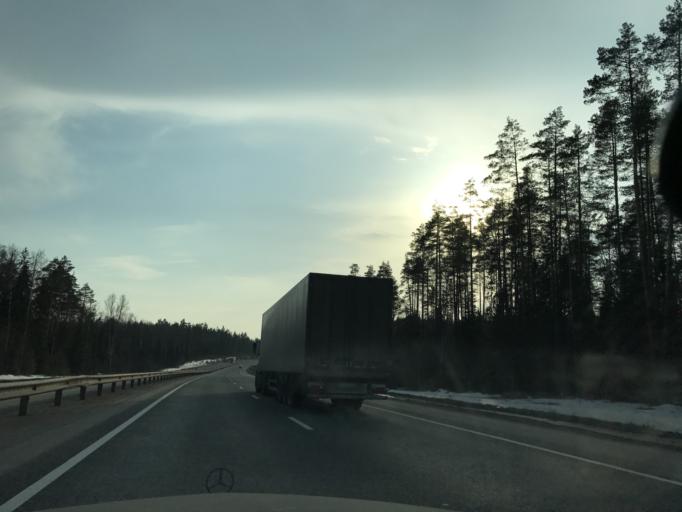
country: RU
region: Vladimir
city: Sudogda
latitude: 56.1516
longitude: 40.9186
